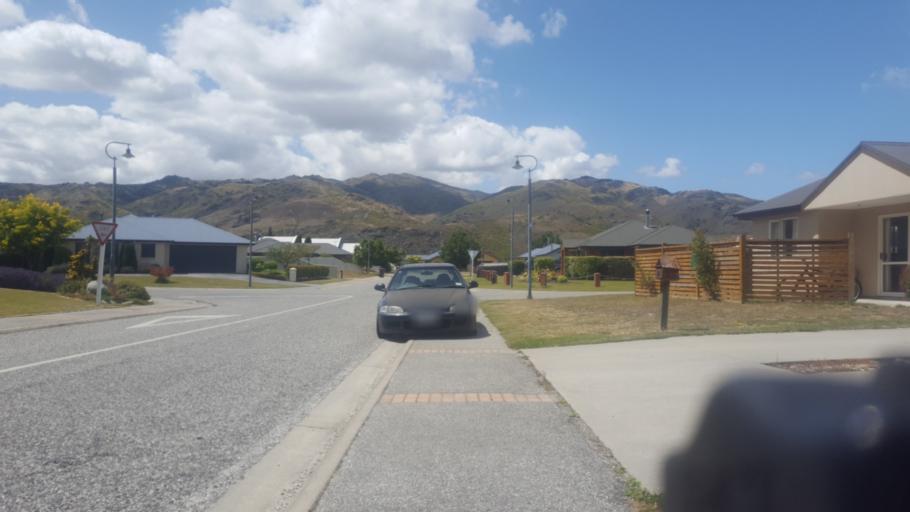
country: NZ
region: Otago
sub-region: Queenstown-Lakes District
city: Wanaka
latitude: -45.0483
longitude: 169.1987
